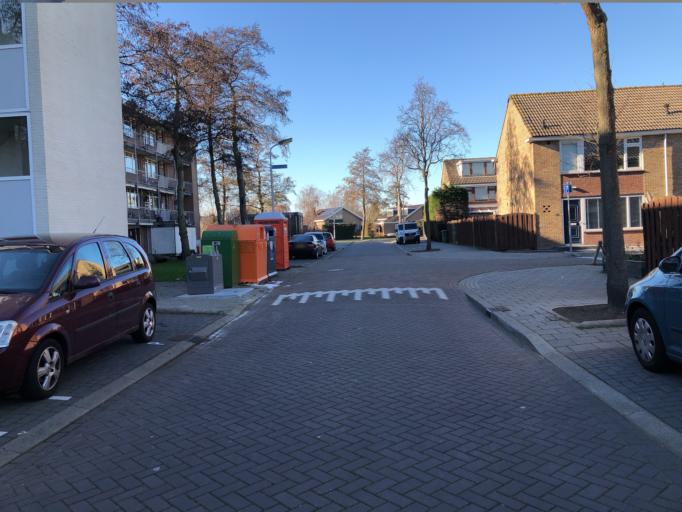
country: NL
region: North Holland
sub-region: Gemeente Uitgeest
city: Uitgeest
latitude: 52.5082
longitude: 4.7586
